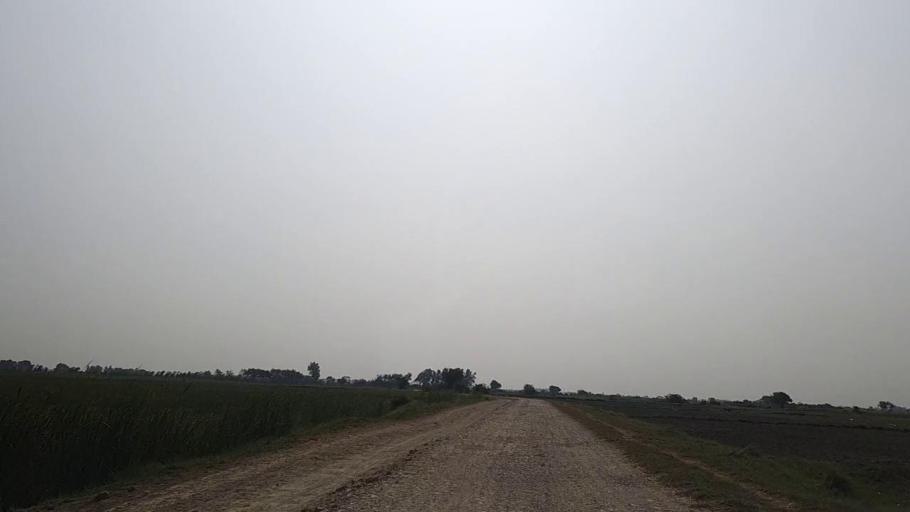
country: PK
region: Sindh
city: Mirpur Sakro
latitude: 24.6384
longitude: 67.7674
